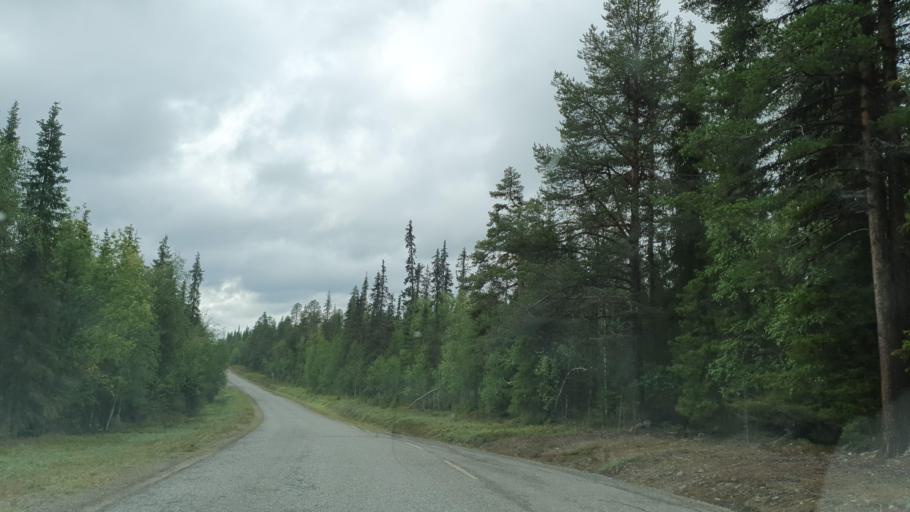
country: FI
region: Lapland
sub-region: Tunturi-Lappi
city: Kittilae
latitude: 67.7392
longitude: 24.2844
